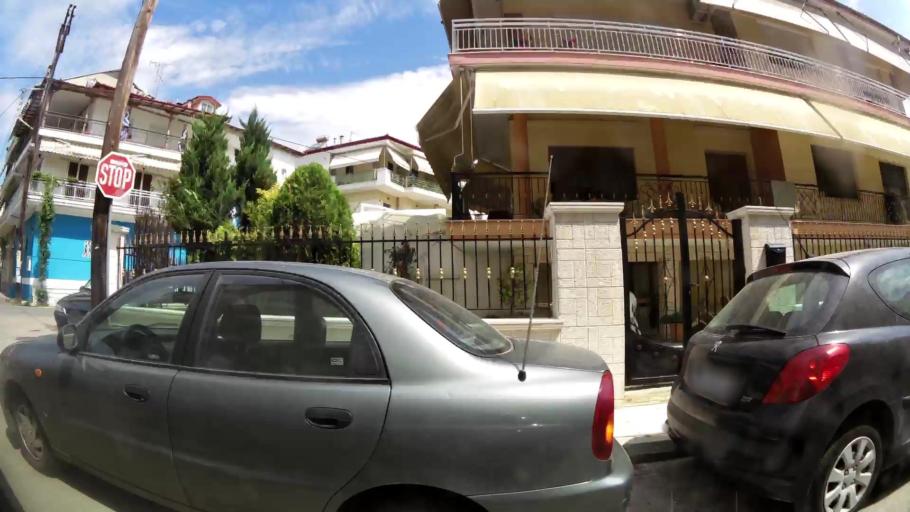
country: GR
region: Central Macedonia
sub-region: Nomos Pierias
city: Katerini
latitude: 40.2711
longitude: 22.4944
